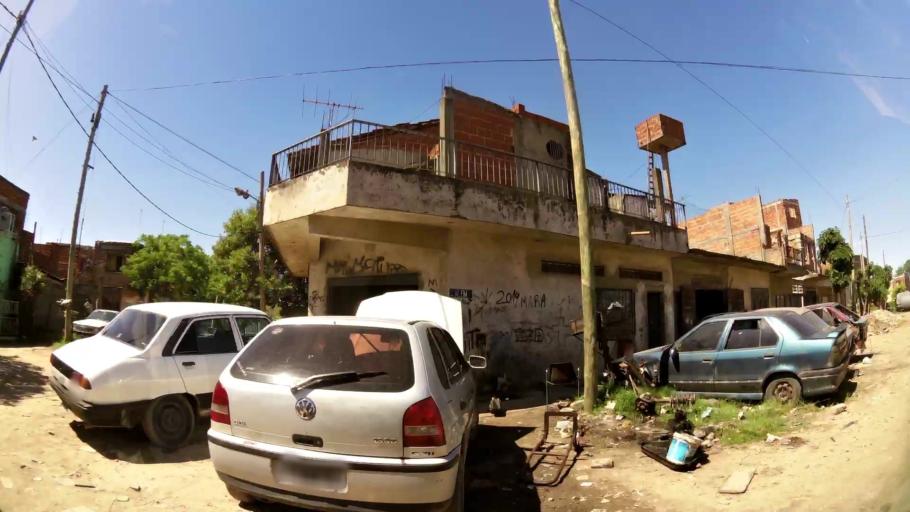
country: AR
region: Buenos Aires
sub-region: Partido de Quilmes
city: Quilmes
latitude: -34.7300
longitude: -58.3117
